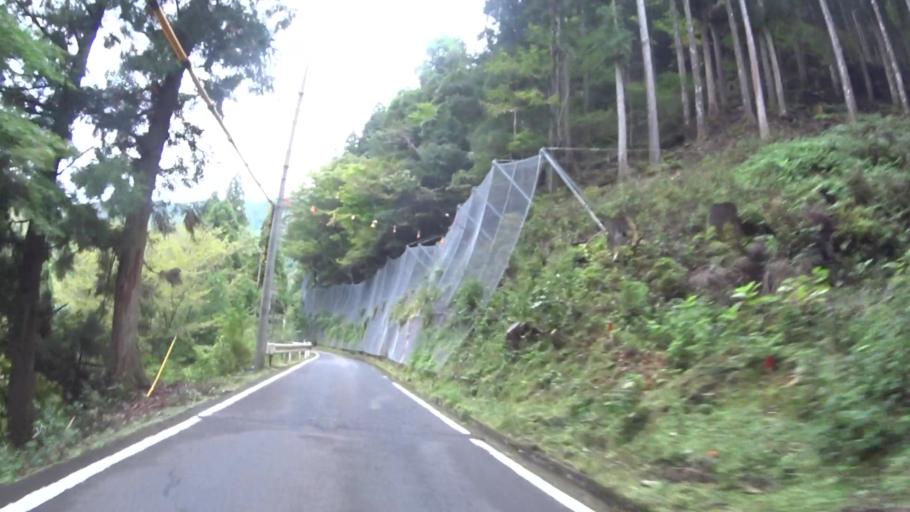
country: JP
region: Fukui
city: Obama
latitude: 35.3144
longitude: 135.6854
